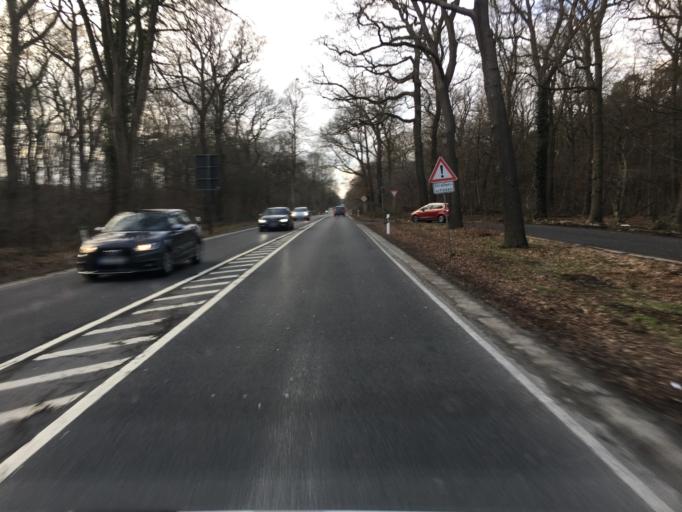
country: DE
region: North Rhine-Westphalia
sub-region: Regierungsbezirk Koln
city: Rath
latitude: 50.9079
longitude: 7.1357
